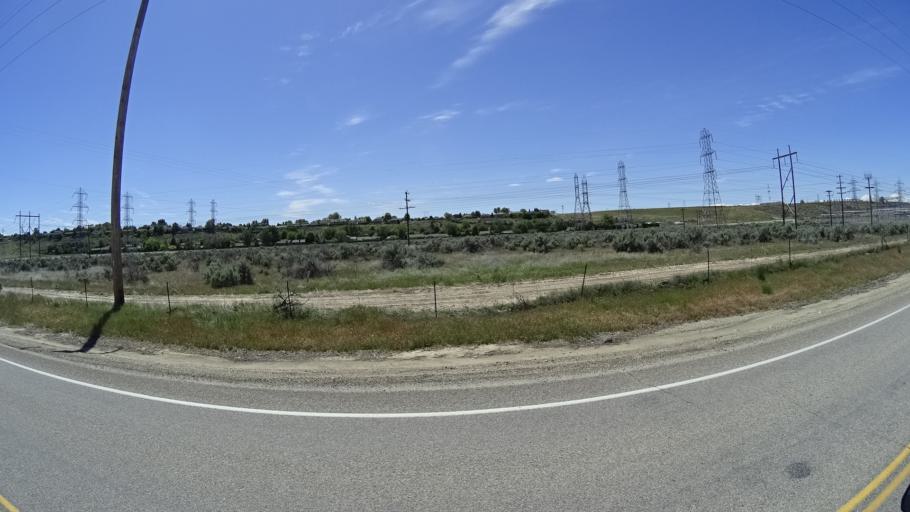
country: US
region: Idaho
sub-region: Ada County
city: Boise
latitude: 43.5606
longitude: -116.1508
